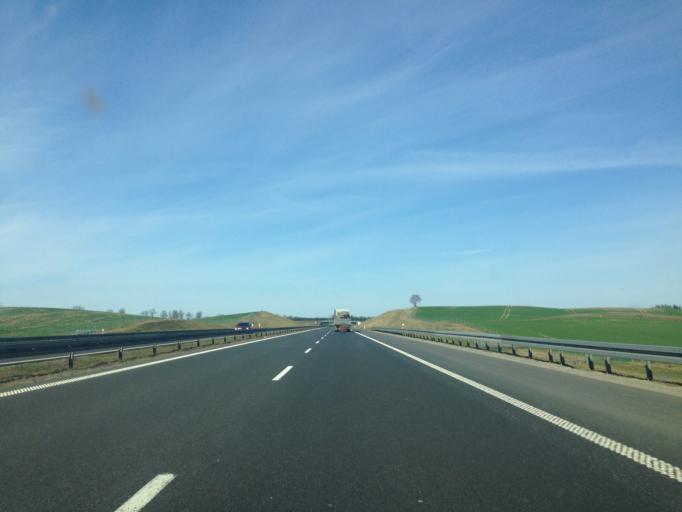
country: PL
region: Pomeranian Voivodeship
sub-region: Powiat starogardzki
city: Smetowo Graniczne
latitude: 53.7893
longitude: 18.6276
